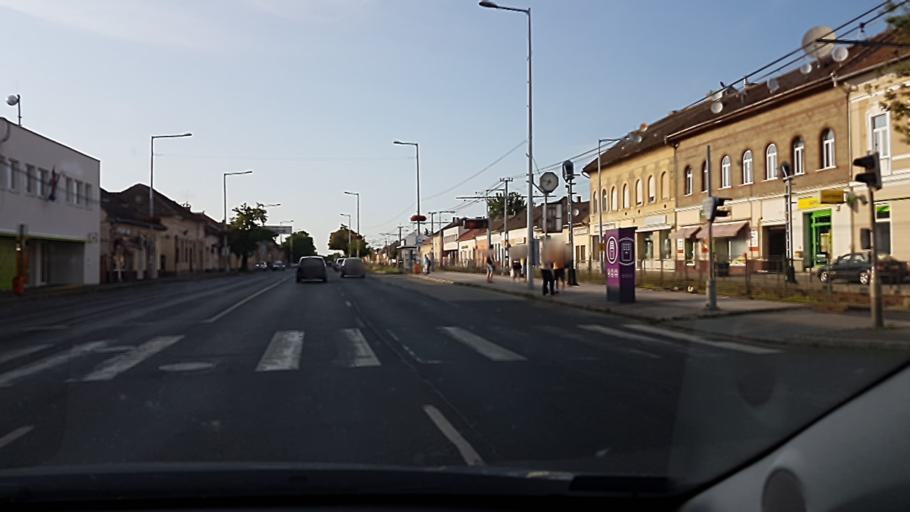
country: HU
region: Budapest
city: Budapest XXIII. keruelet
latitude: 47.3993
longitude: 19.1146
